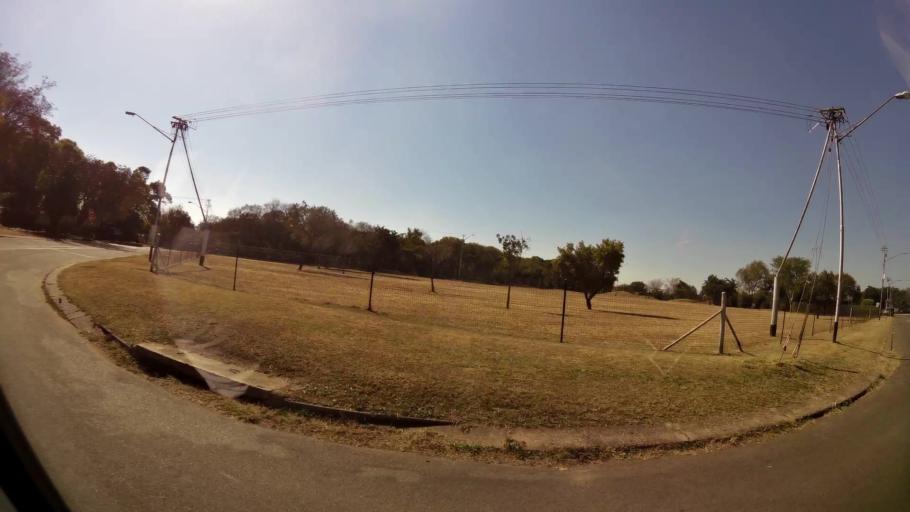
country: ZA
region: Gauteng
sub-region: City of Tshwane Metropolitan Municipality
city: Pretoria
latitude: -25.7699
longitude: 28.2392
